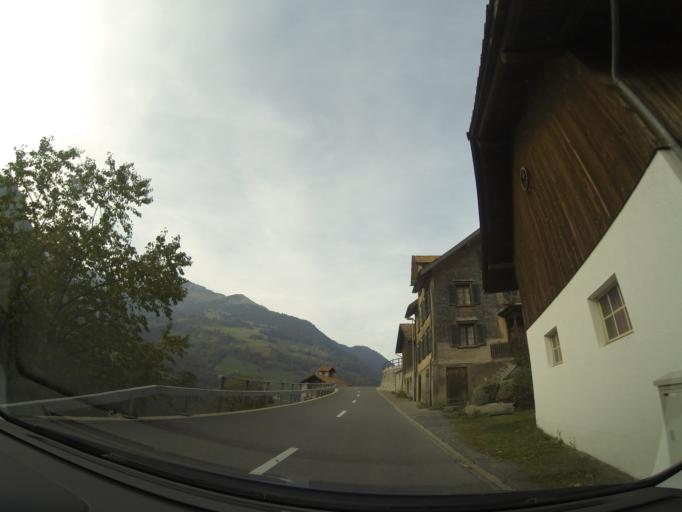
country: CH
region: Saint Gallen
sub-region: Wahlkreis Sarganserland
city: Bad Ragaz
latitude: 46.9574
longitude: 9.4849
